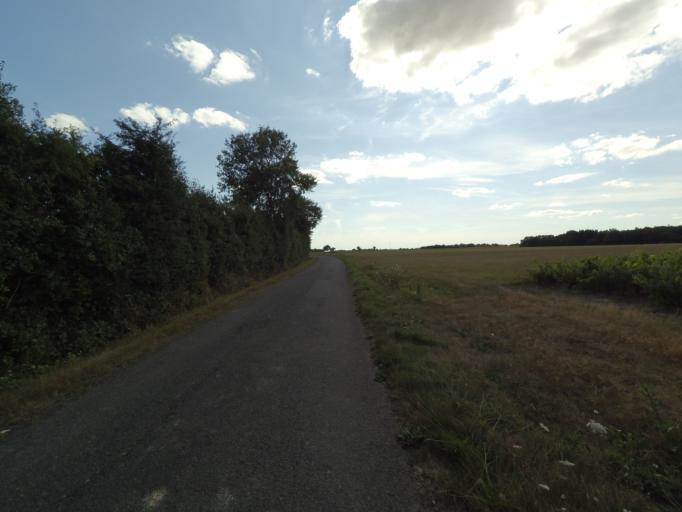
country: FR
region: Pays de la Loire
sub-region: Departement de la Loire-Atlantique
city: Vieillevigne
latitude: 46.9632
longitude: -1.4400
